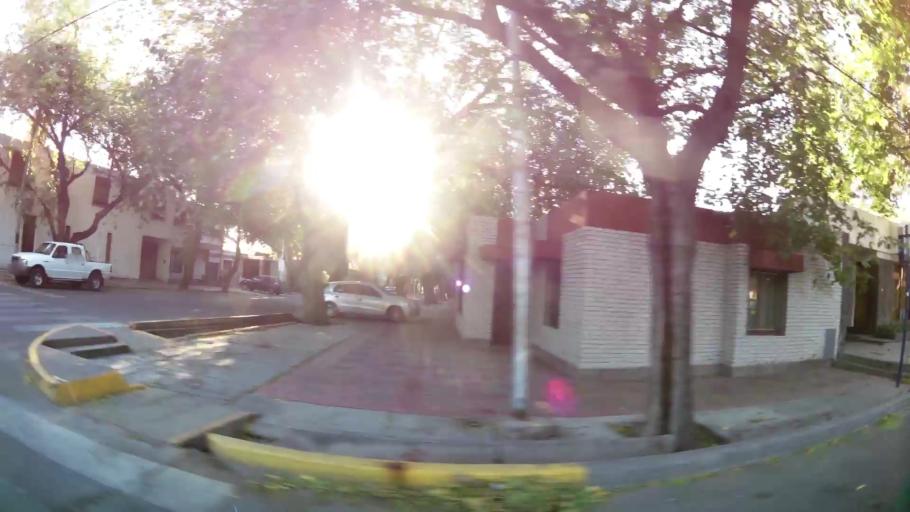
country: AR
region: Mendoza
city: Las Heras
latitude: -32.8632
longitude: -68.8380
